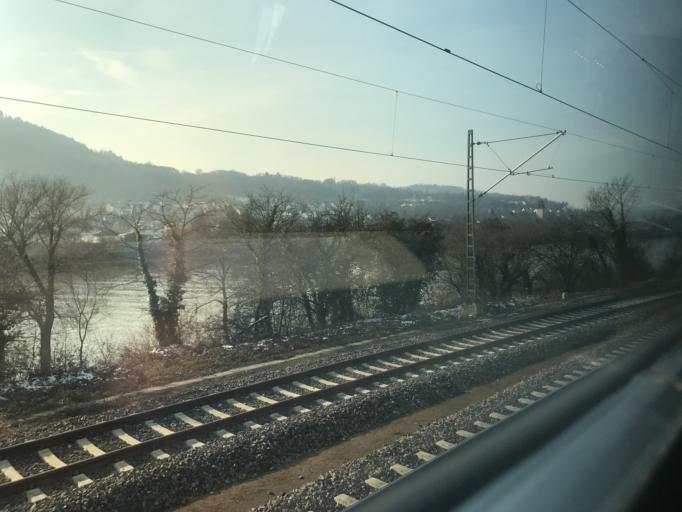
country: DE
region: Rheinland-Pfalz
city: Wasserliesch
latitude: 49.7080
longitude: 6.5485
